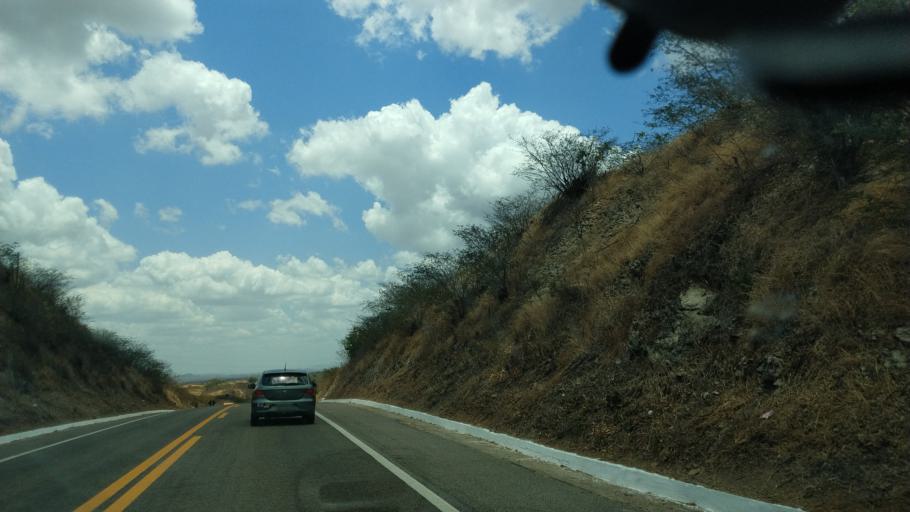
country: BR
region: Rio Grande do Norte
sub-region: Cerro Cora
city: Cerro Cora
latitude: -6.1878
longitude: -36.2383
